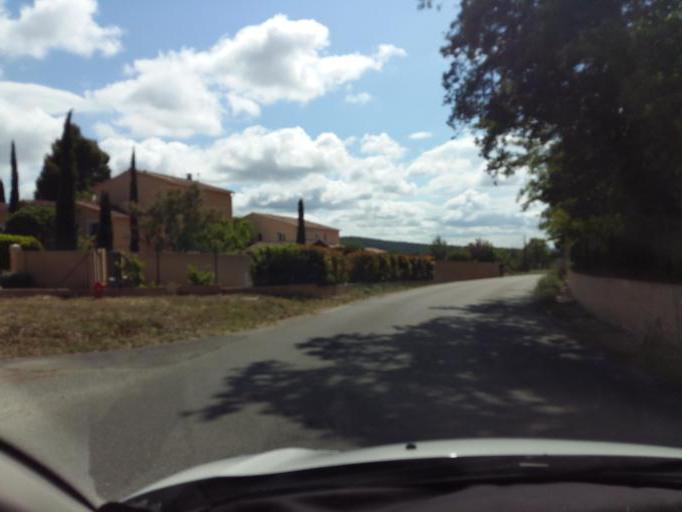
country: FR
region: Provence-Alpes-Cote d'Azur
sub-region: Departement du Vaucluse
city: Robion
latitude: 43.8428
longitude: 5.1018
